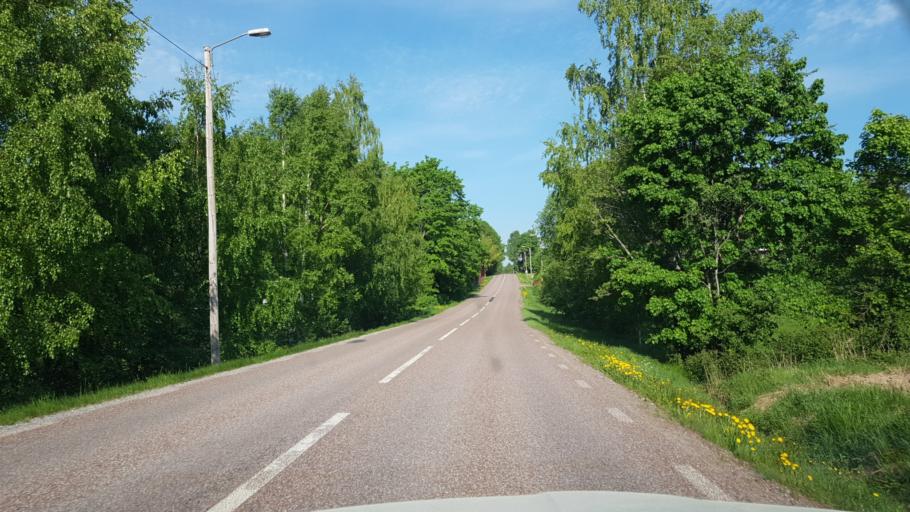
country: SE
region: Dalarna
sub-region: Saters Kommun
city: Saeter
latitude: 60.4143
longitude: 15.7719
